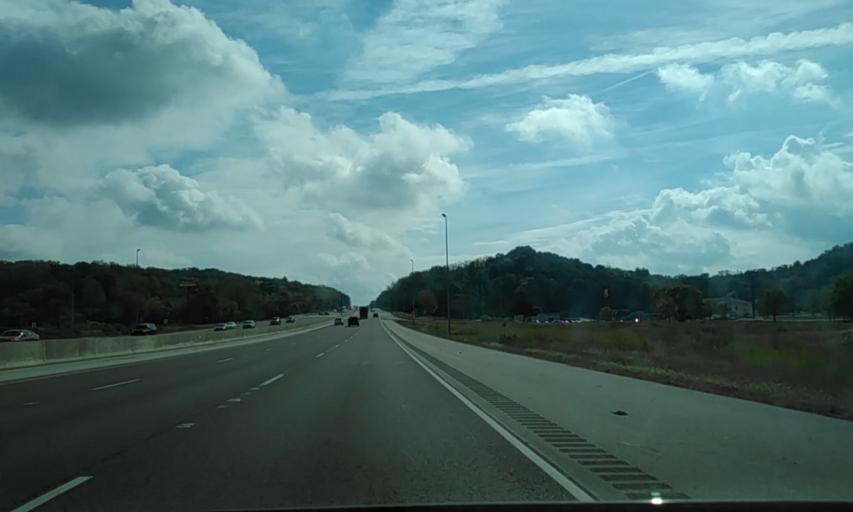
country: US
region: Illinois
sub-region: Saint Clair County
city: Caseyville
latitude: 38.6159
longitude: -90.0494
